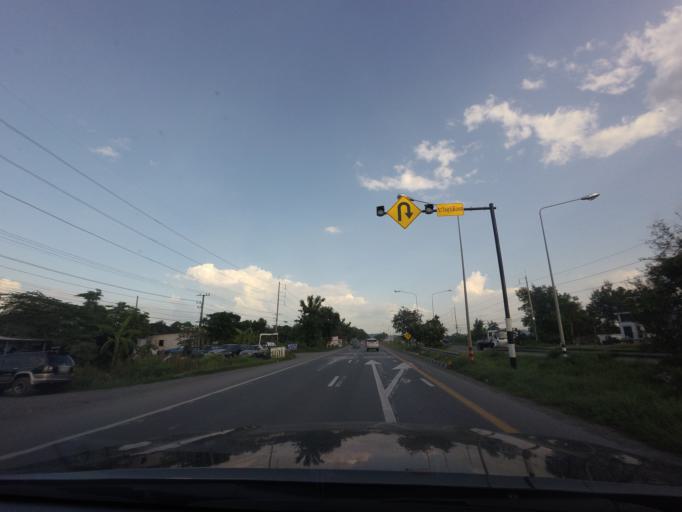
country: TH
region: Sara Buri
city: Saraburi
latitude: 14.5175
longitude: 100.8943
